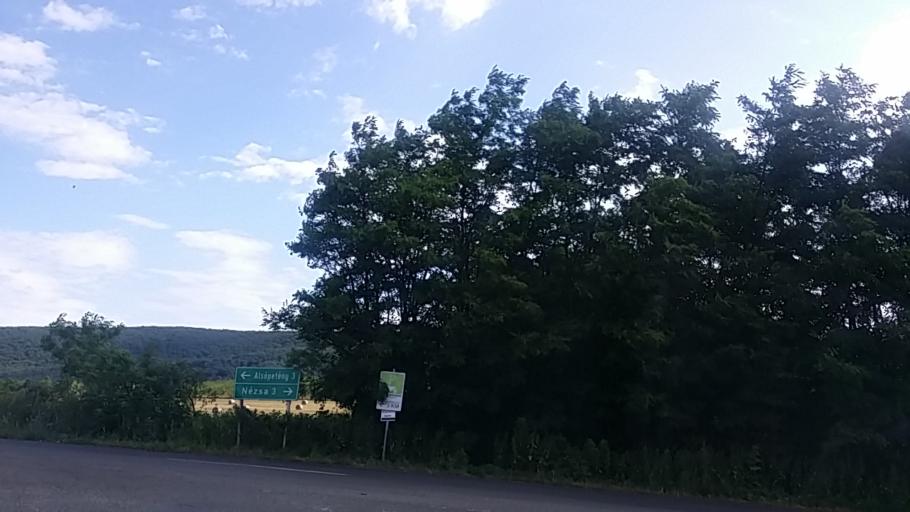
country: HU
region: Nograd
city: Romhany
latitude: 47.8588
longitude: 19.2655
